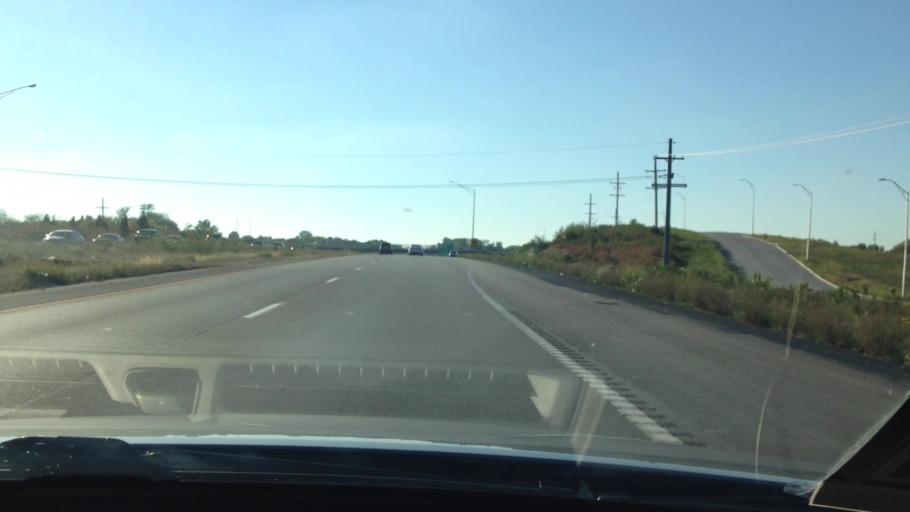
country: US
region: Missouri
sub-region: Platte County
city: Weatherby Lake
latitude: 39.2543
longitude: -94.6251
